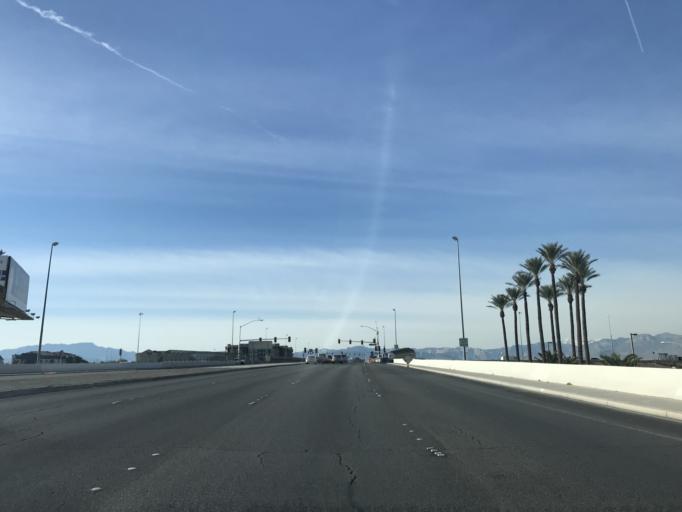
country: US
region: Nevada
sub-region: Clark County
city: Paradise
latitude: 36.0861
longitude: -115.1775
